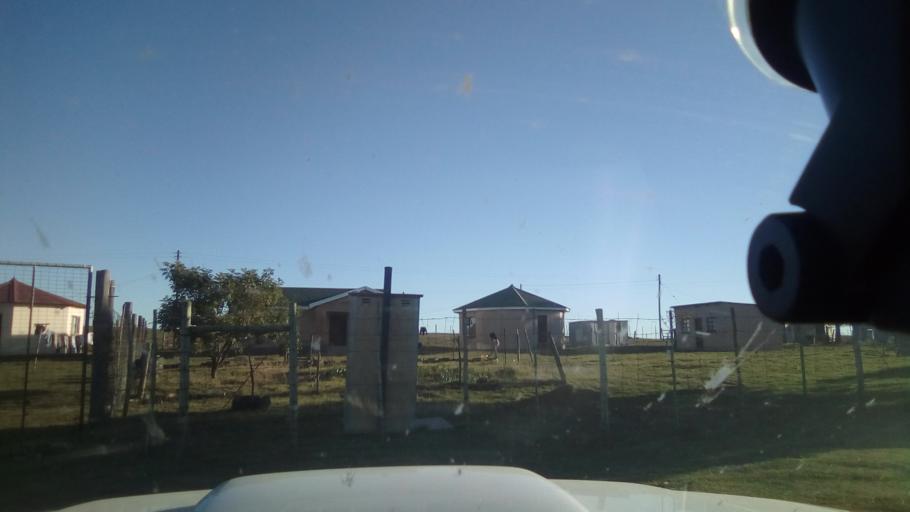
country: ZA
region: Eastern Cape
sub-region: Buffalo City Metropolitan Municipality
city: Bhisho
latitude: -32.9524
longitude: 27.2933
